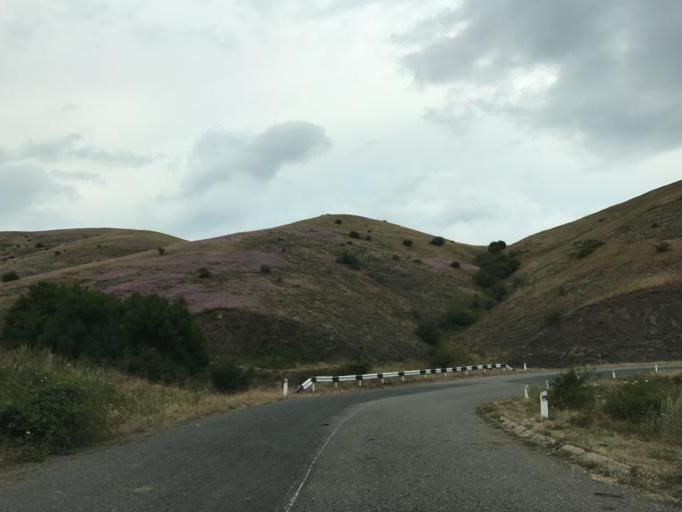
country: AZ
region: Susa
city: Shushi
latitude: 39.6924
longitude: 46.6404
